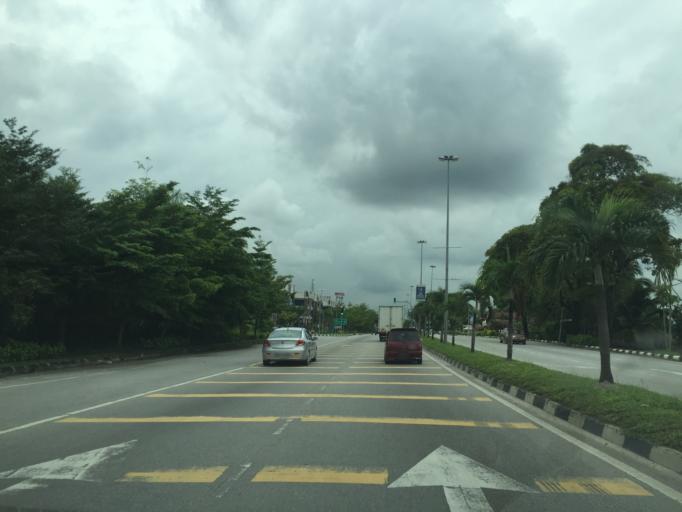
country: MY
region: Perak
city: Ipoh
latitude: 4.5347
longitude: 101.1278
